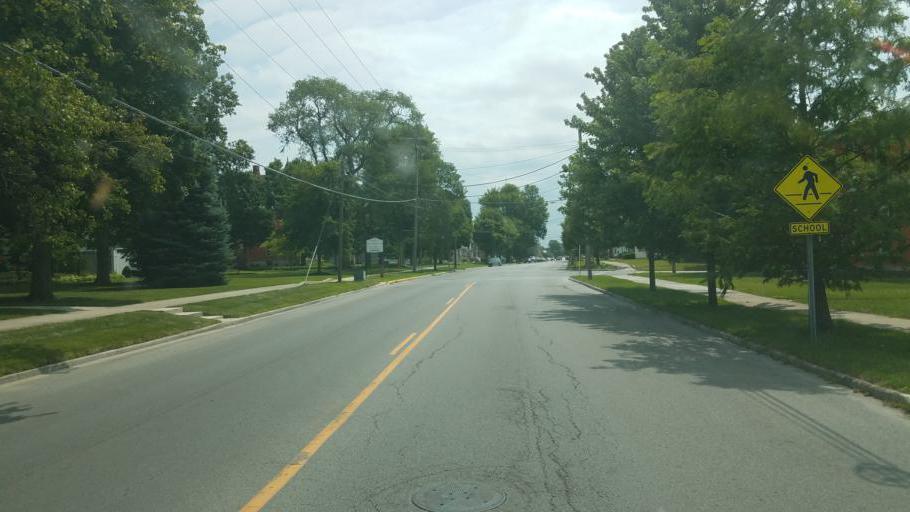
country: US
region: Ohio
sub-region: Wyandot County
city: Carey
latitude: 40.9533
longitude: -83.3874
